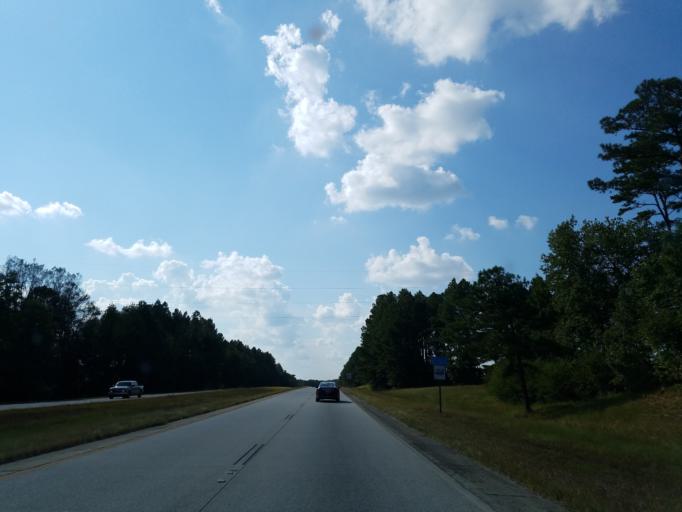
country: US
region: Georgia
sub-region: Barrow County
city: Statham
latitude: 33.9454
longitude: -83.5753
